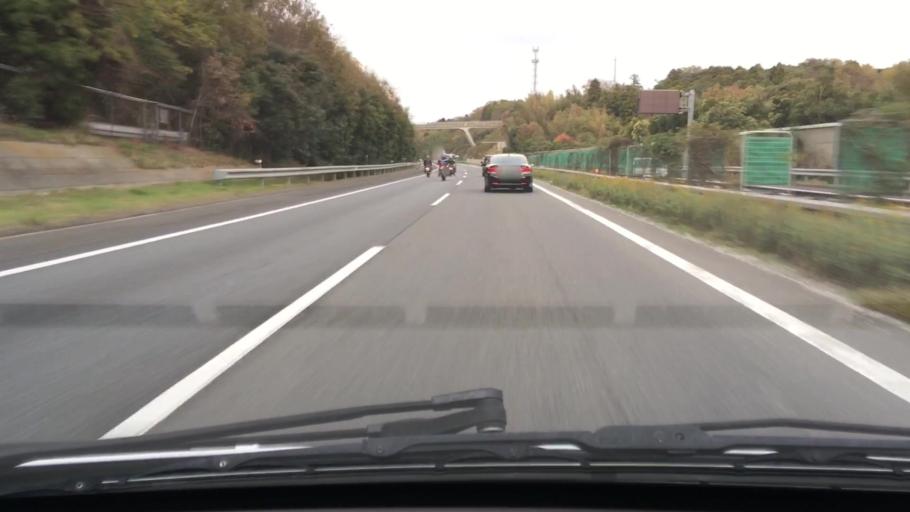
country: JP
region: Chiba
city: Ichihara
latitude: 35.4303
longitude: 140.0471
